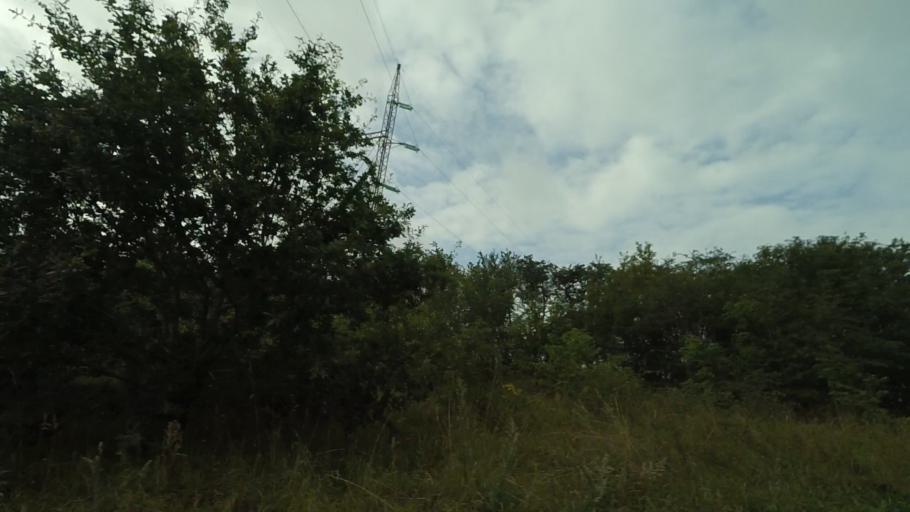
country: DK
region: Central Jutland
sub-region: Syddjurs Kommune
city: Ronde
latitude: 56.3382
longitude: 10.4699
